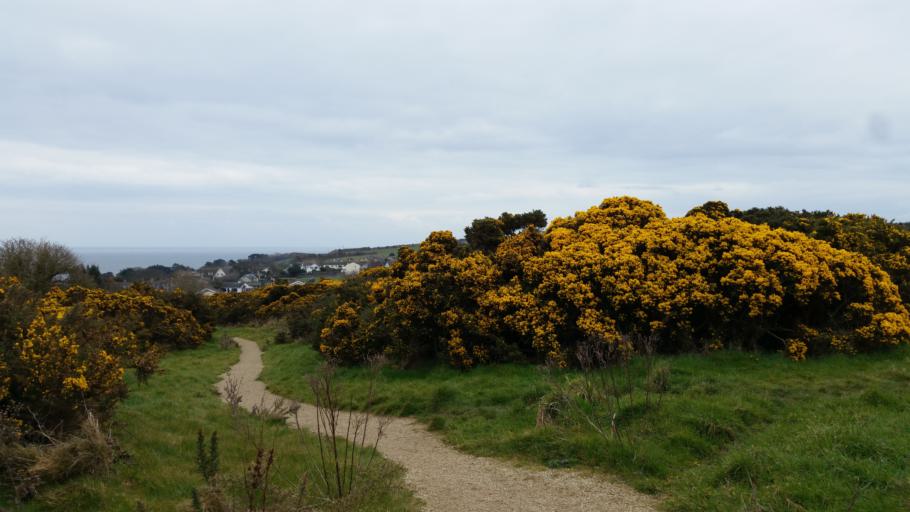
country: IE
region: Leinster
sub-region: Fingal County
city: Howth
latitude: 53.3798
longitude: -6.0685
